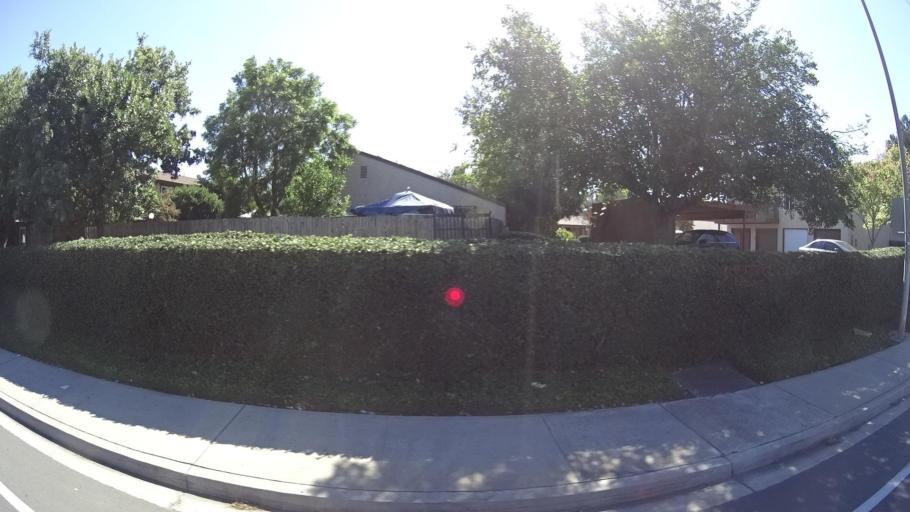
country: US
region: California
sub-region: San Diego County
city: La Presa
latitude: 32.6973
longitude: -117.0208
